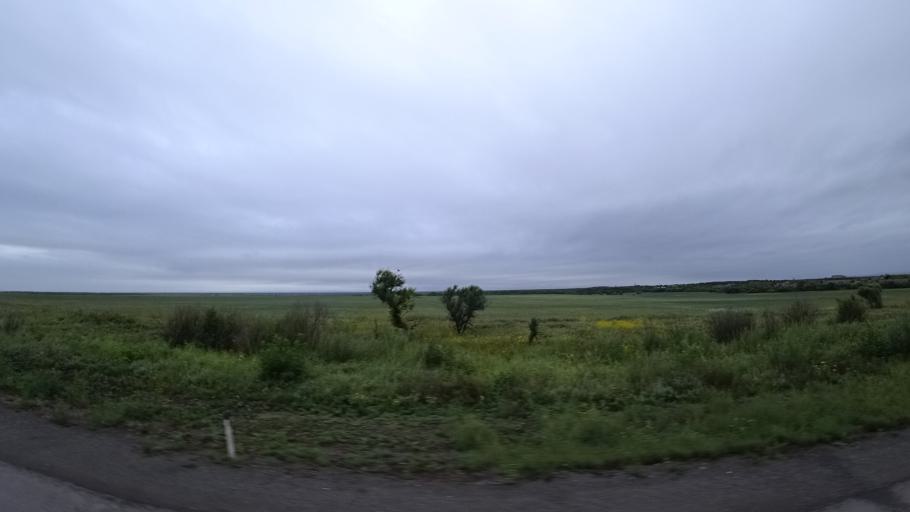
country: RU
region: Primorskiy
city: Chernigovka
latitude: 44.3062
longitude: 132.5389
